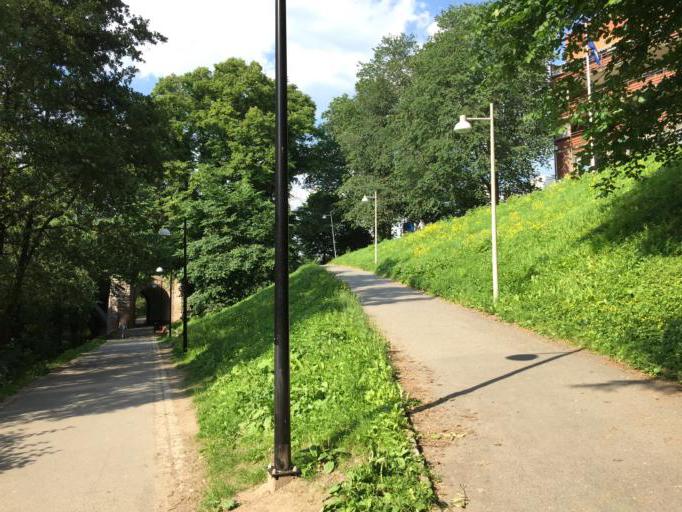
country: NO
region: Oslo
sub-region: Oslo
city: Oslo
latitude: 59.9276
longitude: 10.7552
